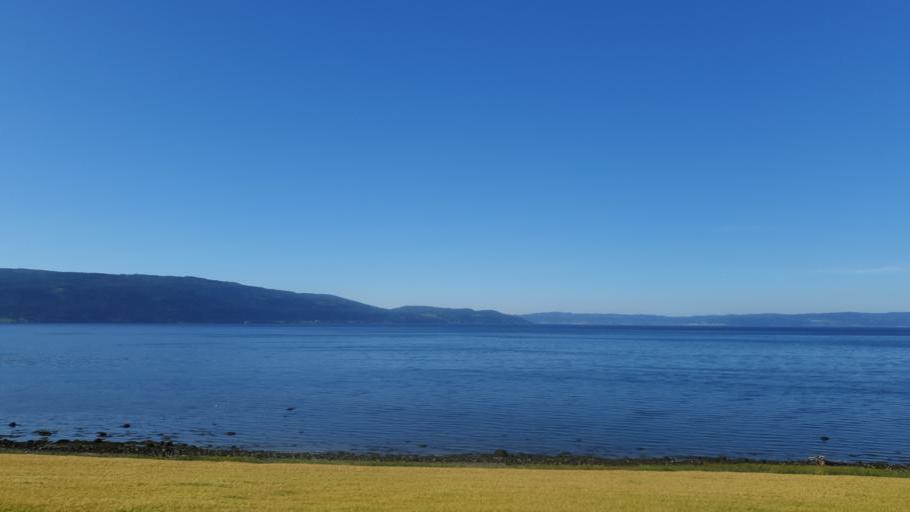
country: NO
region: Sor-Trondelag
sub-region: Skaun
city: Borsa
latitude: 63.3457
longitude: 10.0093
